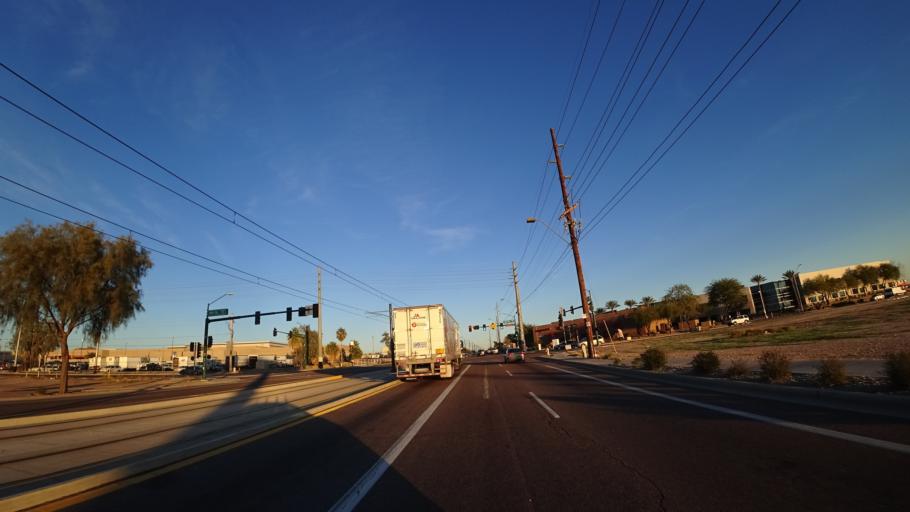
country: US
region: Arizona
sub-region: Maricopa County
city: Tempe Junction
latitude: 33.4474
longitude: -111.9792
